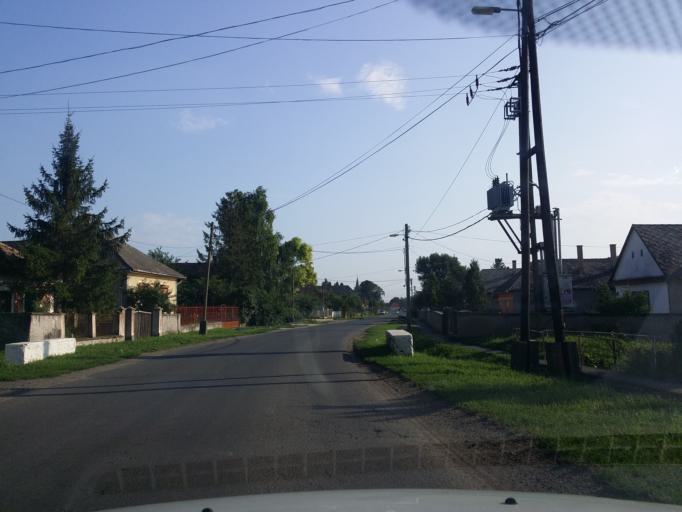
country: HU
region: Borsod-Abauj-Zemplen
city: Gonc
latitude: 48.4198
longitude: 21.2333
